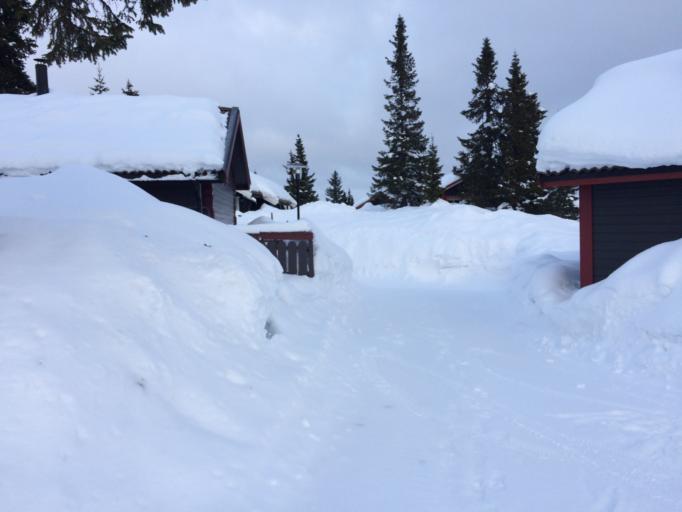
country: NO
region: Oppland
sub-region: Gausdal
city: Segalstad bru
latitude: 61.3321
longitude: 10.0905
